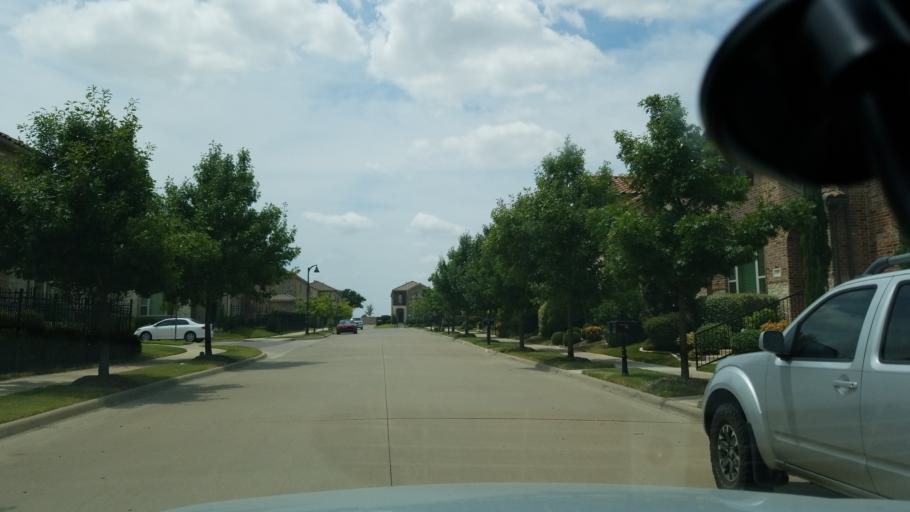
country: US
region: Texas
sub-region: Dallas County
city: Farmers Branch
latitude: 32.9000
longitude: -96.9433
